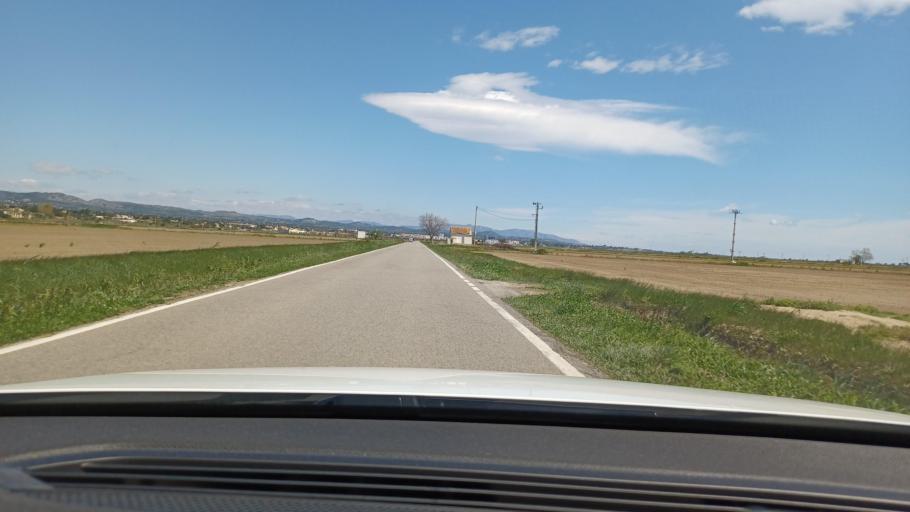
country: ES
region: Catalonia
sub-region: Provincia de Tarragona
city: L'Ampolla
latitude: 40.7819
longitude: 0.6910
